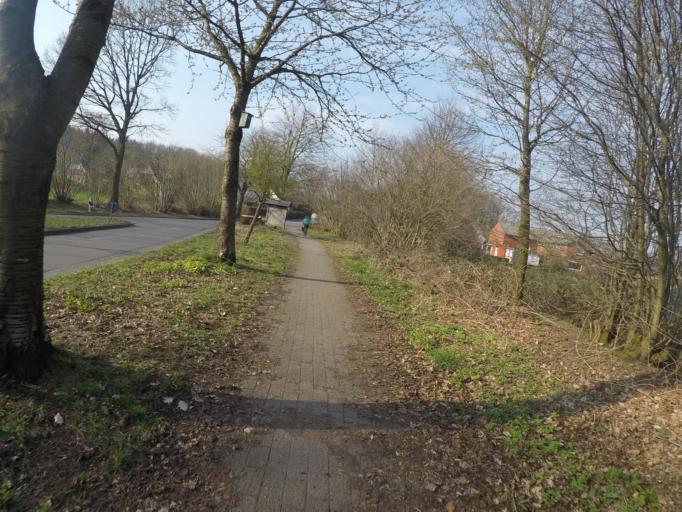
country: DE
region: Schleswig-Holstein
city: Wittenborn
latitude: 53.9197
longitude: 10.2216
